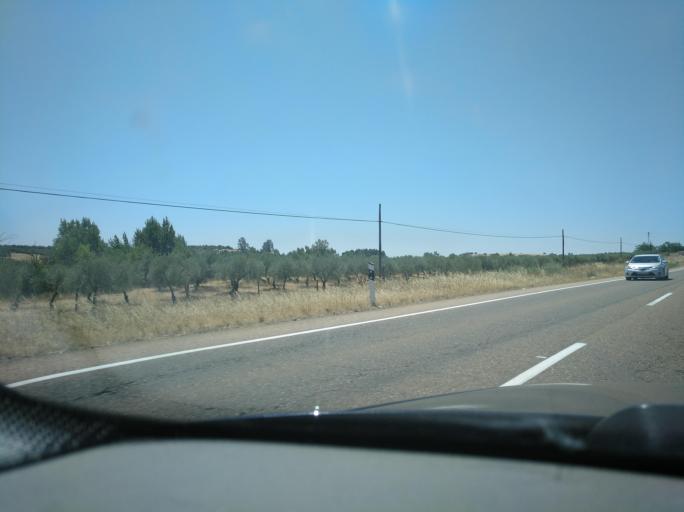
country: ES
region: Extremadura
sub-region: Provincia de Badajoz
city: Olivenza
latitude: 38.7348
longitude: -7.0687
